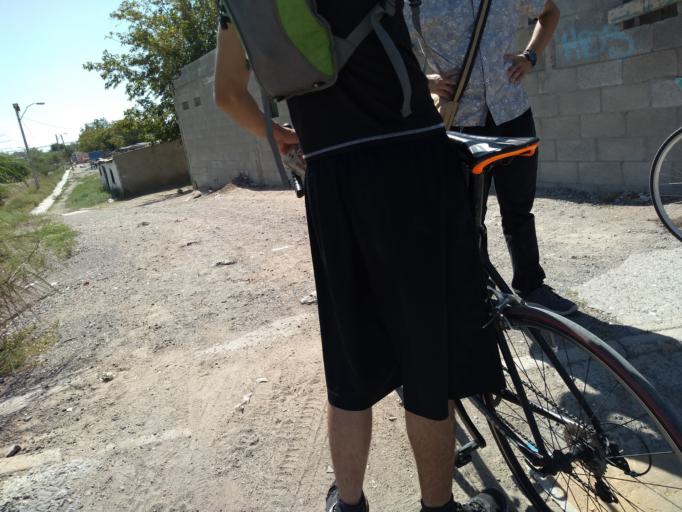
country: US
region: Texas
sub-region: El Paso County
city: El Paso
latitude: 31.7494
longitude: -106.4953
